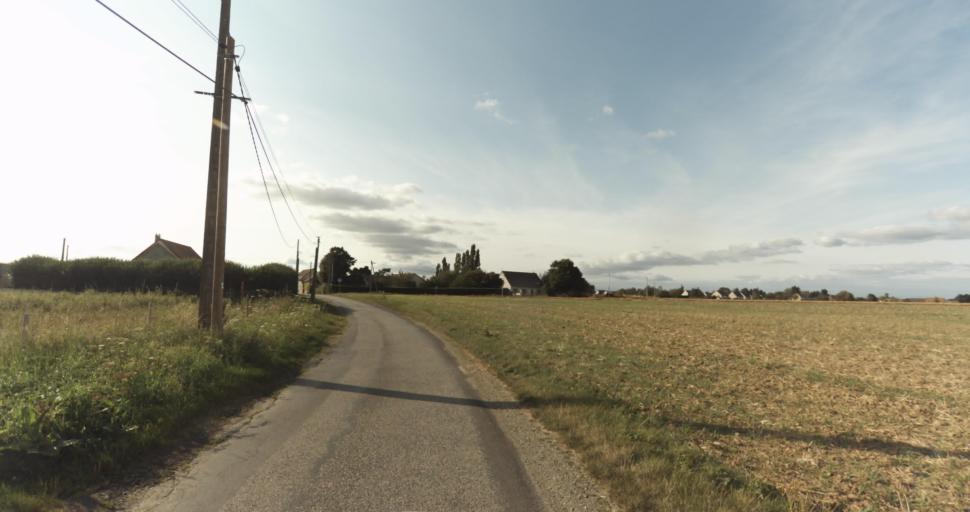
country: FR
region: Haute-Normandie
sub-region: Departement de l'Eure
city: La Couture-Boussey
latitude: 48.9010
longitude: 1.3486
